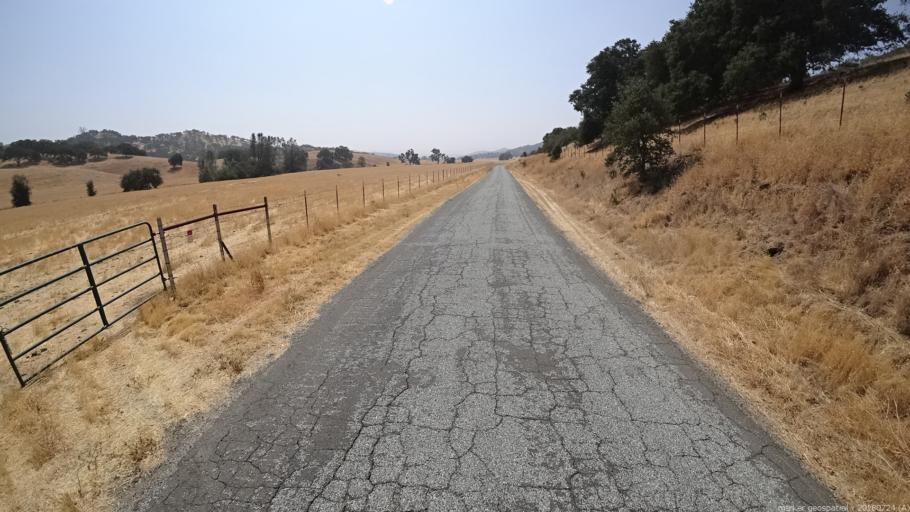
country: US
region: California
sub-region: San Luis Obispo County
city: San Miguel
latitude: 36.0477
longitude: -120.6666
